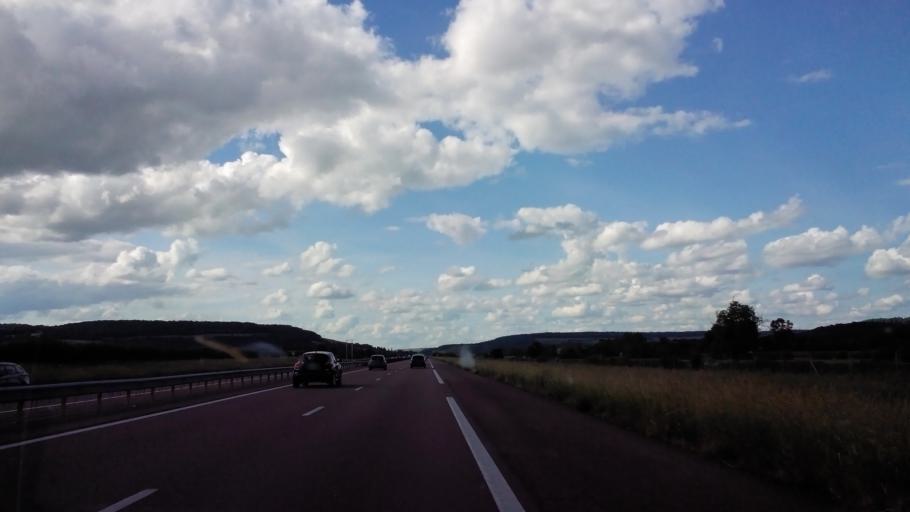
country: FR
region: Bourgogne
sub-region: Departement de la Cote-d'Or
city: Pouilly-en-Auxois
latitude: 47.2763
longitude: 4.5111
